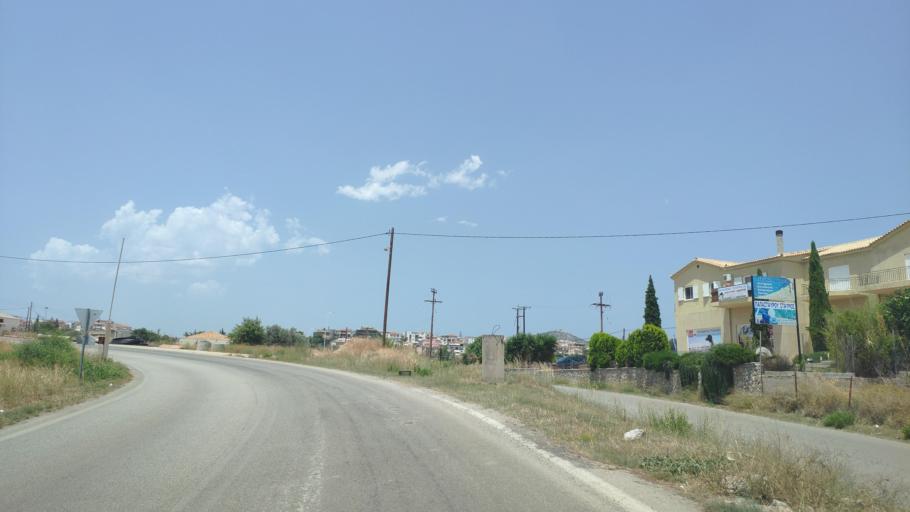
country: GR
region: Peloponnese
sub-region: Nomos Argolidos
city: Kranidi
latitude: 37.3696
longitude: 23.1628
